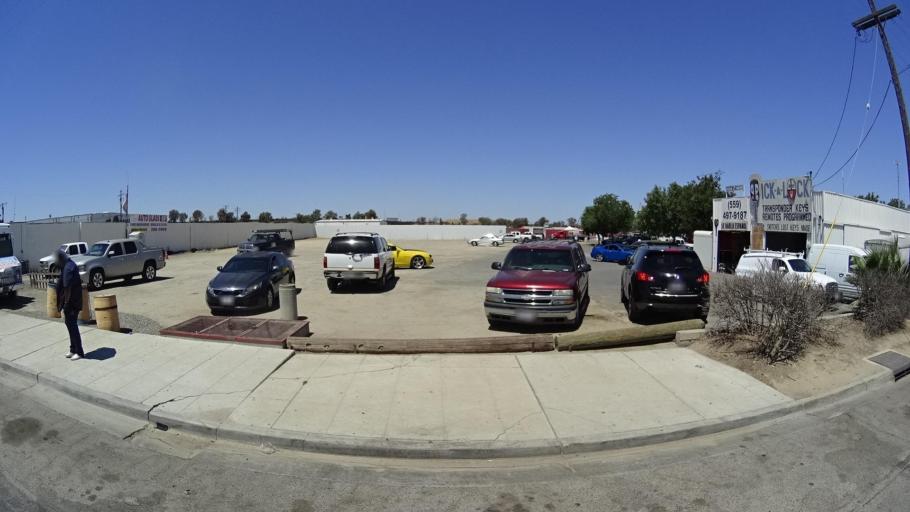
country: US
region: California
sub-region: Fresno County
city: Easton
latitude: 36.6859
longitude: -119.7457
